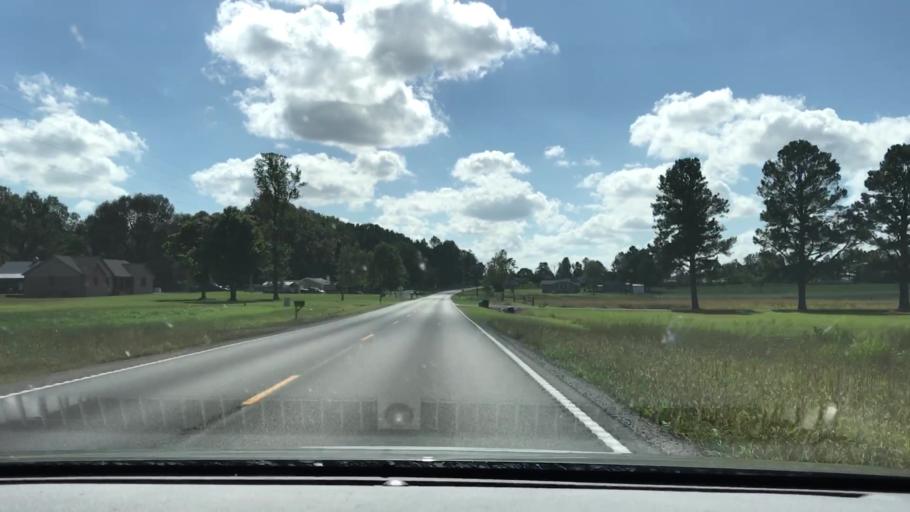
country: US
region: Kentucky
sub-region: Graves County
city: Mayfield
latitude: 36.8595
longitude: -88.5720
